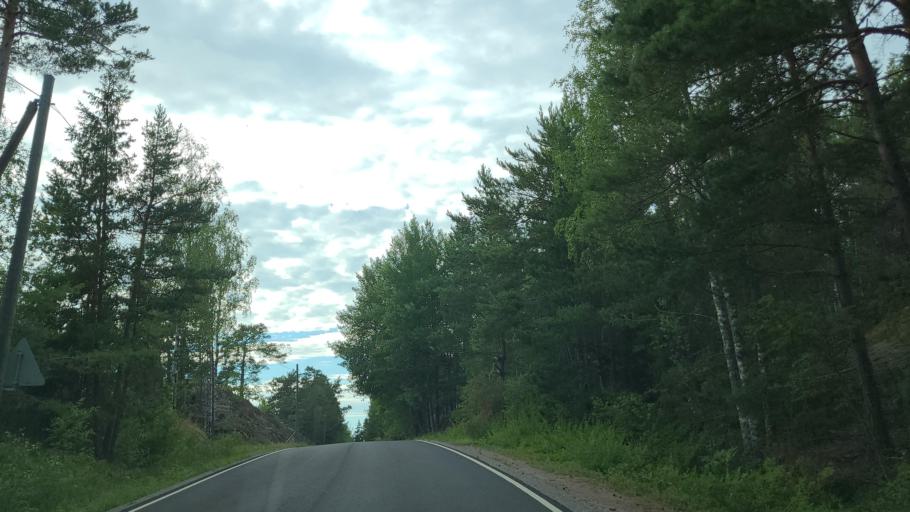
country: FI
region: Varsinais-Suomi
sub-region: Turku
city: Rymaettylae
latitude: 60.3192
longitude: 21.9610
